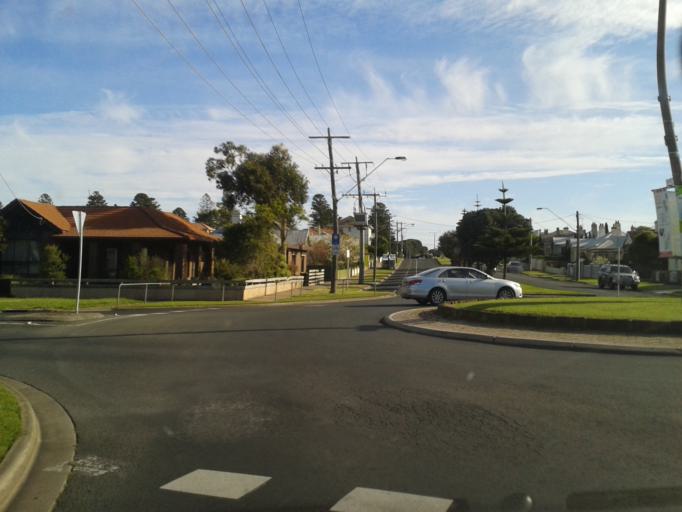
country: AU
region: Victoria
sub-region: Warrnambool
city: Warrnambool
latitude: -38.3846
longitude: 142.4861
